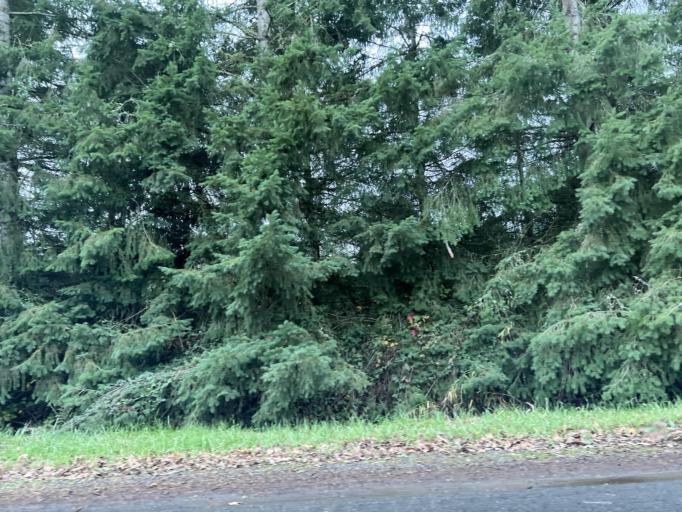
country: US
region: Oregon
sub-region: Polk County
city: Independence
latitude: 44.8125
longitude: -123.0877
